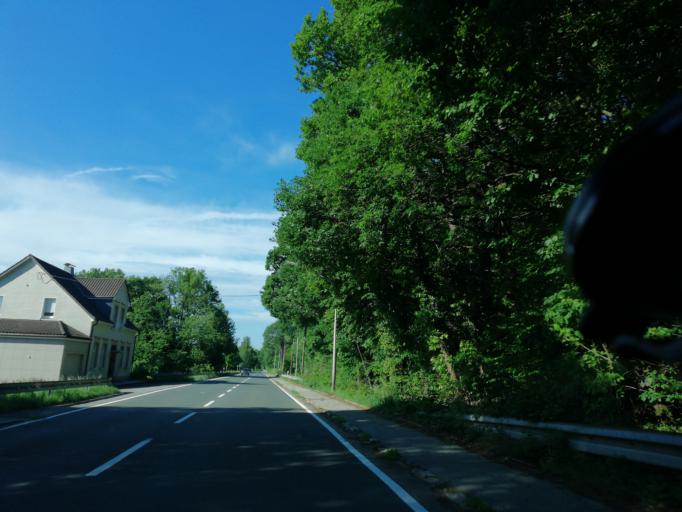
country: DE
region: North Rhine-Westphalia
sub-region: Regierungsbezirk Arnsberg
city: Schwelm
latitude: 51.3148
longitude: 7.2917
